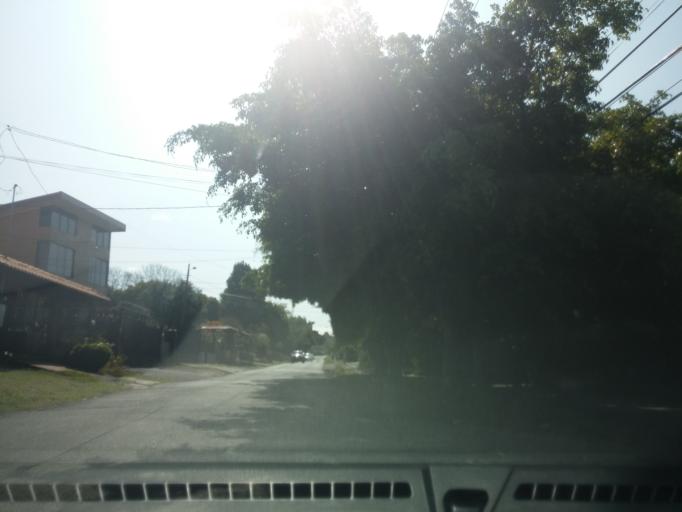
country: CR
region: Heredia
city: Mercedes
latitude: 10.0137
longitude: -84.1432
